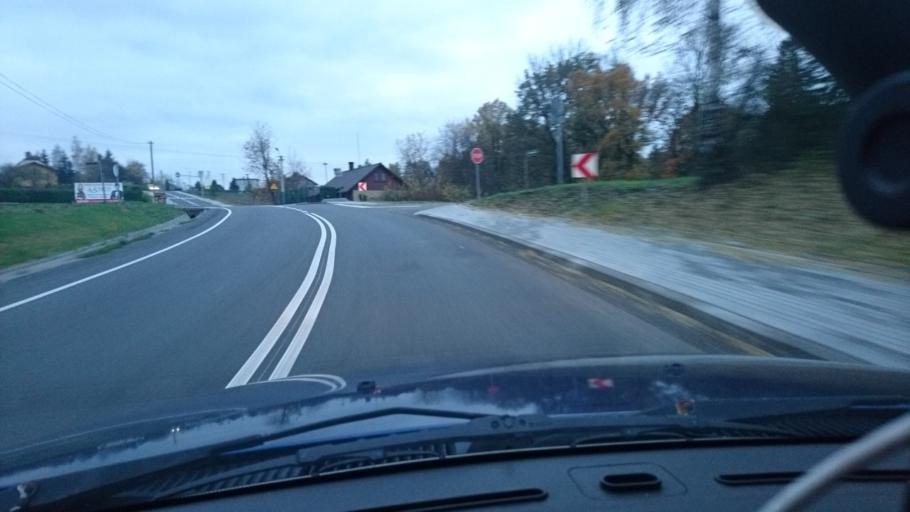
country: PL
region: Silesian Voivodeship
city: Janowice
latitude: 49.9052
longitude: 19.0835
